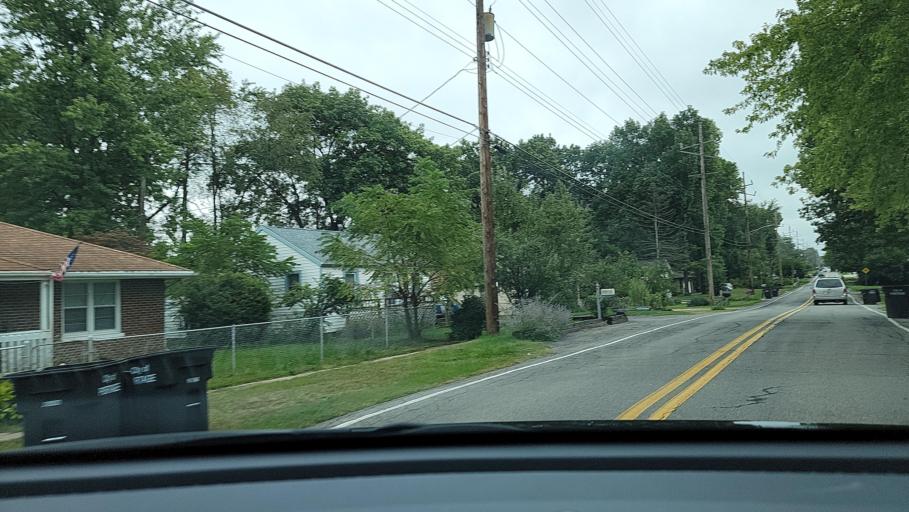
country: US
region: Indiana
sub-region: Porter County
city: Portage
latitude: 41.5718
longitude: -87.1987
